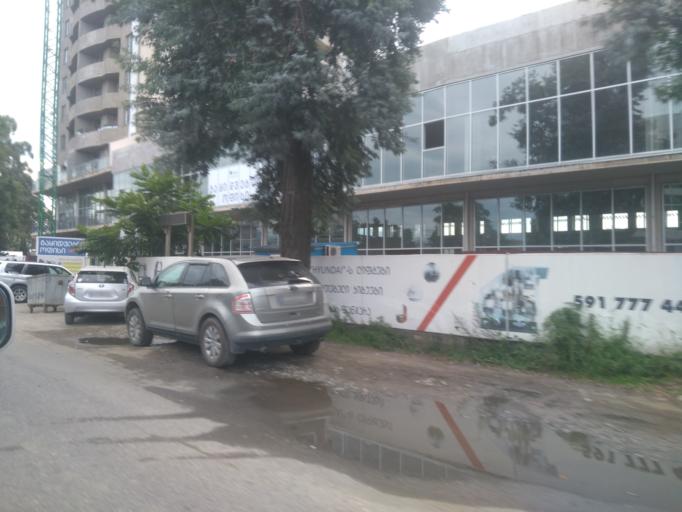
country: GE
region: Ajaria
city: Batumi
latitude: 41.6226
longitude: 41.6147
